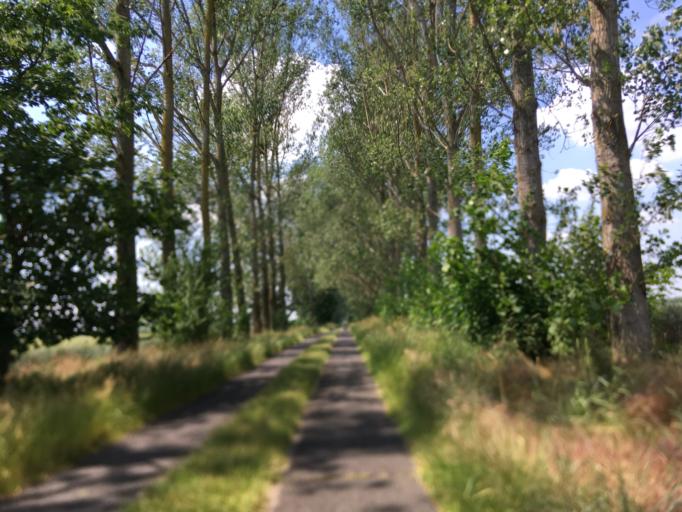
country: DE
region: Brandenburg
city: Werftpfuhl
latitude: 52.6894
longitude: 13.7549
